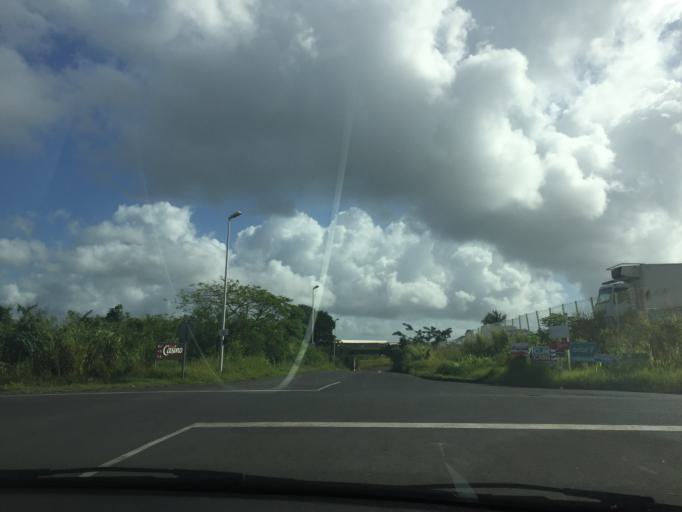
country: GP
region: Guadeloupe
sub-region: Guadeloupe
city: Baie-Mahault
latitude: 16.2437
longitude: -61.5732
